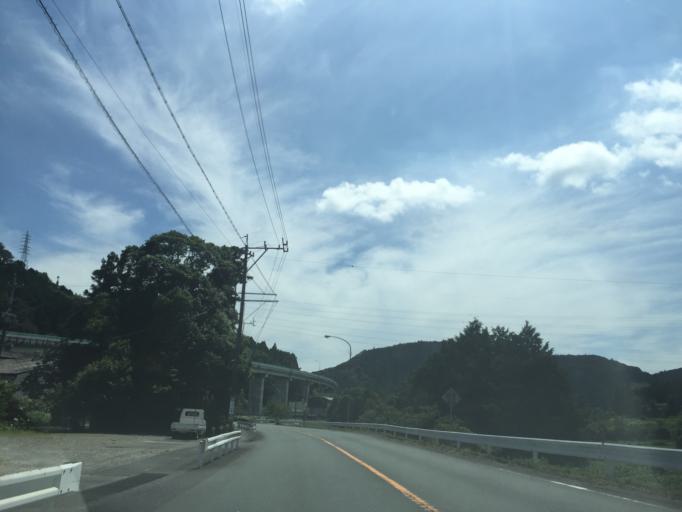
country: JP
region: Shizuoka
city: Kanaya
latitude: 34.8079
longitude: 138.0794
